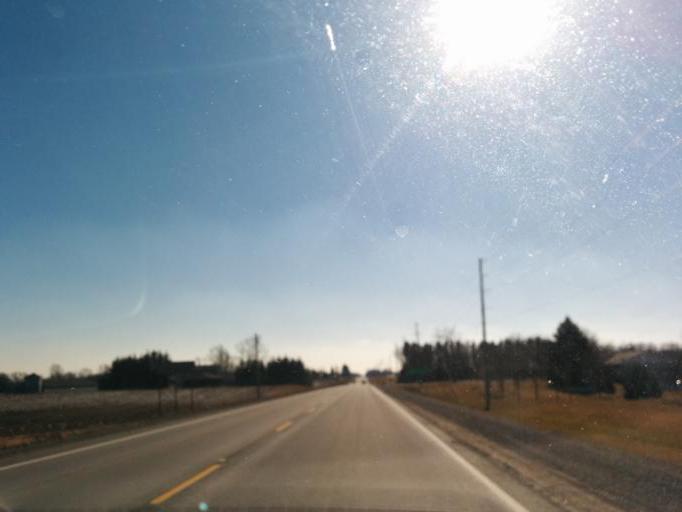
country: CA
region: Ontario
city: Brant
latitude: 43.0014
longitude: -80.3660
